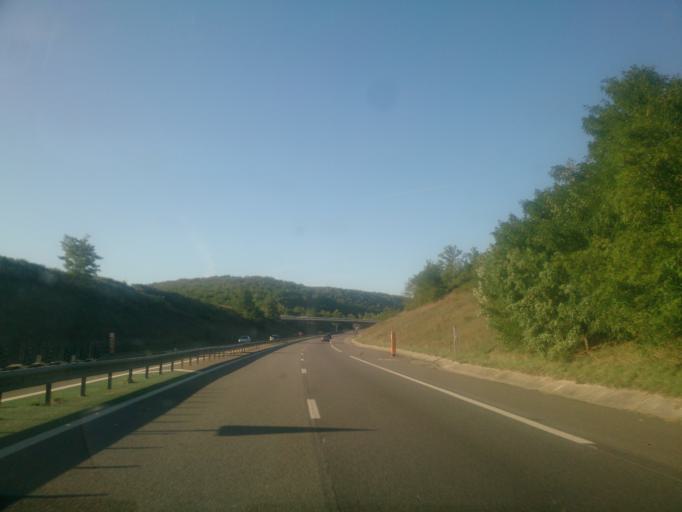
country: FR
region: Midi-Pyrenees
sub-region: Departement du Lot
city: Cahors
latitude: 44.4616
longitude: 1.5021
